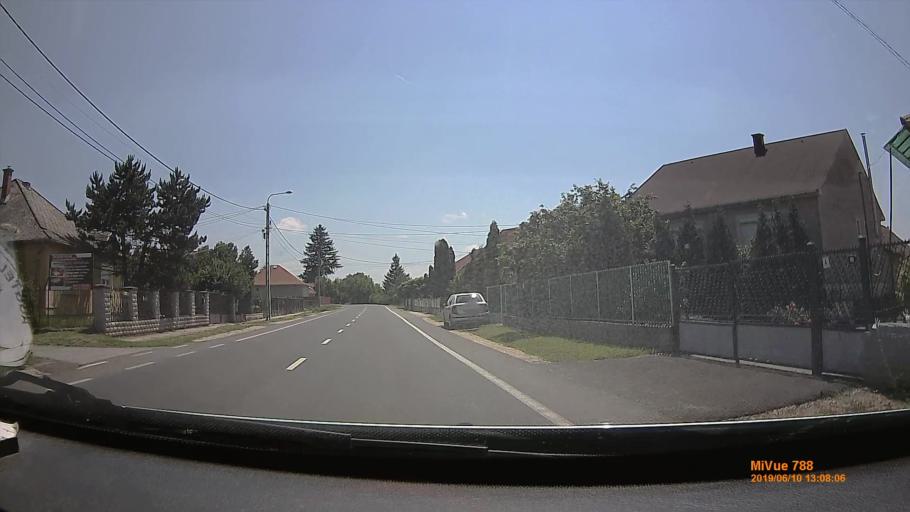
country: HU
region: Borsod-Abauj-Zemplen
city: Gesztely
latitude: 48.0822
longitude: 20.9707
